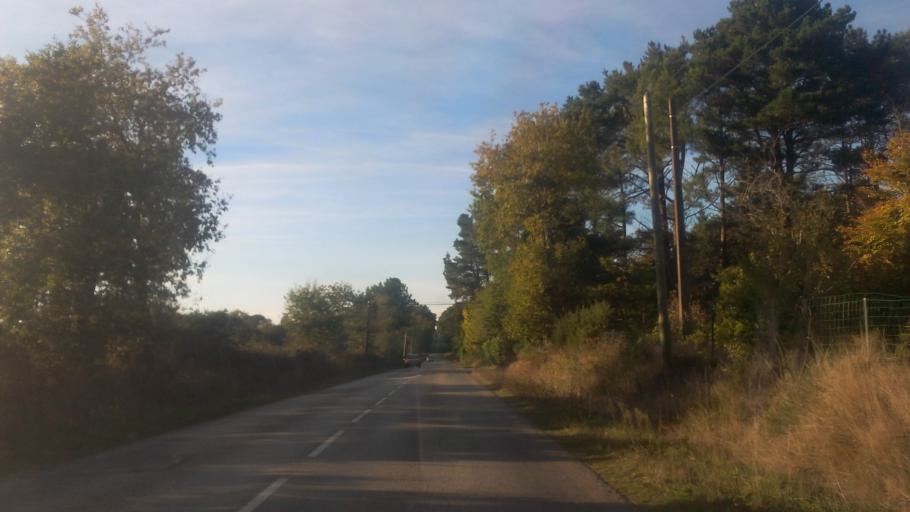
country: FR
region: Brittany
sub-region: Departement du Morbihan
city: La Vraie-Croix
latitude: 47.7054
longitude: -2.5521
